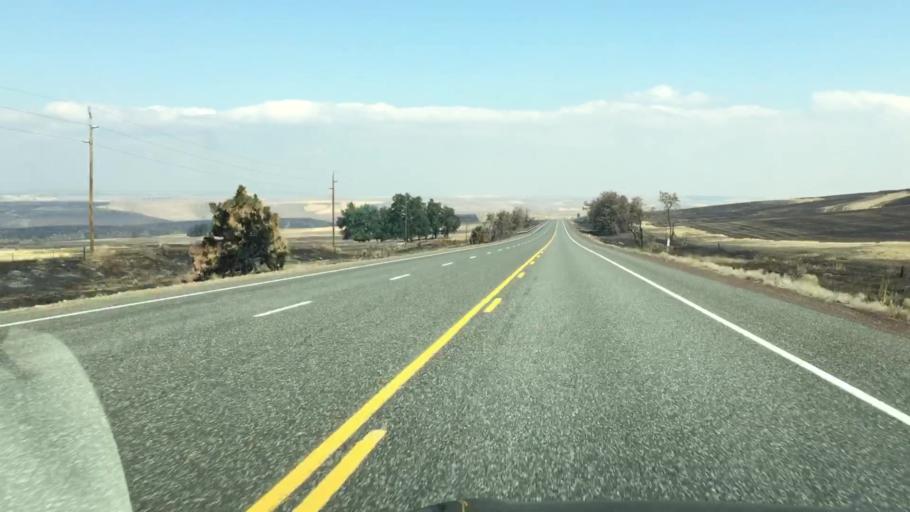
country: US
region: Oregon
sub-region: Wasco County
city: The Dalles
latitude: 45.3799
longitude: -121.1421
